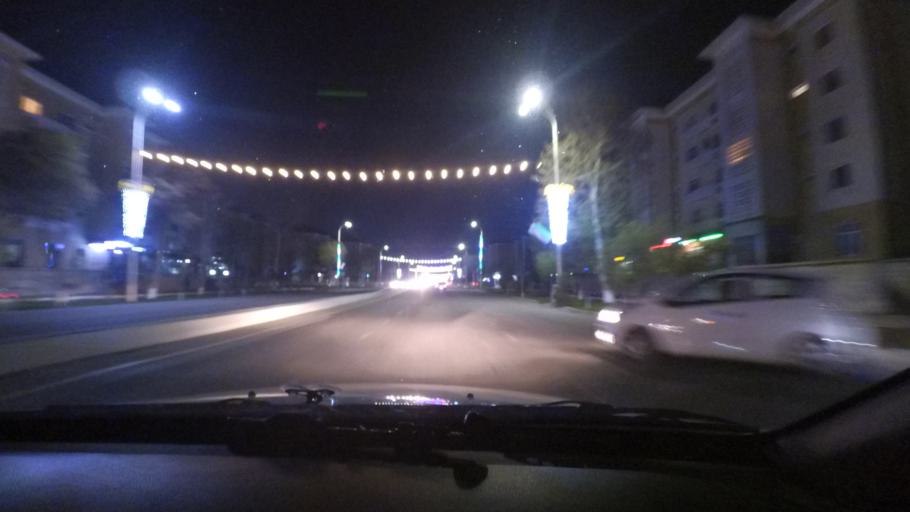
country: UZ
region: Bukhara
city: Bukhara
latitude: 39.7703
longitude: 64.4482
